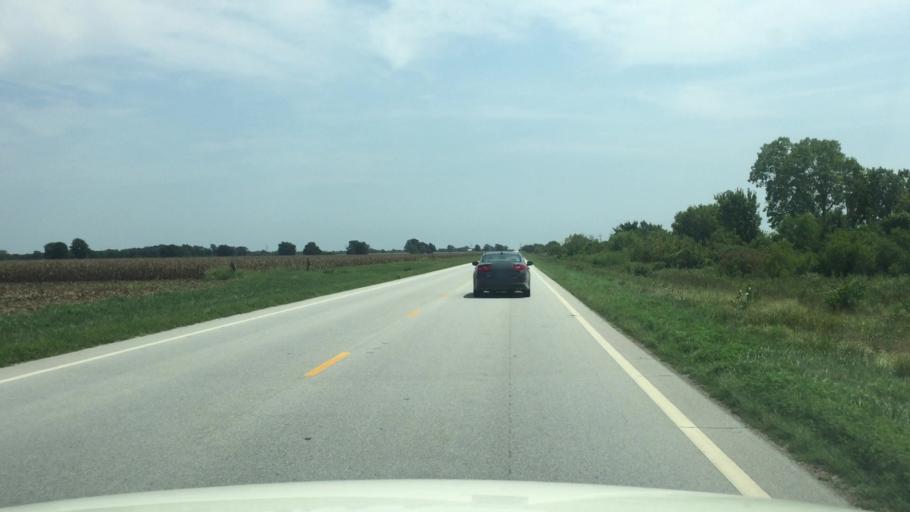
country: US
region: Kansas
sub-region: Cherokee County
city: Columbus
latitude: 37.1792
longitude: -94.9326
